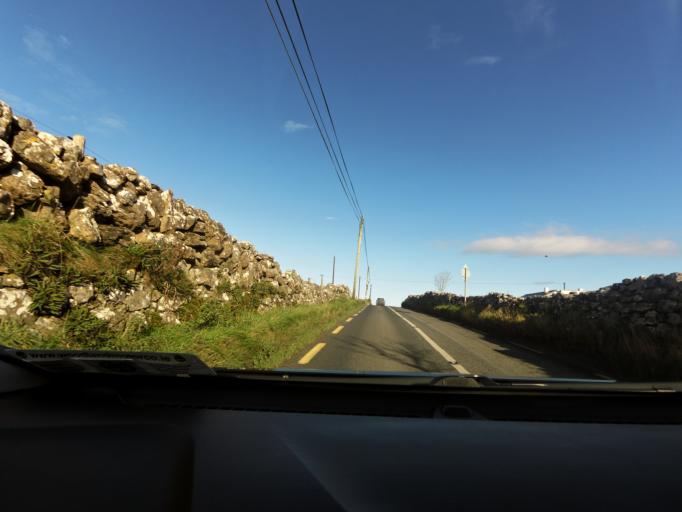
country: IE
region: Connaught
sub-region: County Galway
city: Moycullen
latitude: 53.4917
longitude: -9.0805
